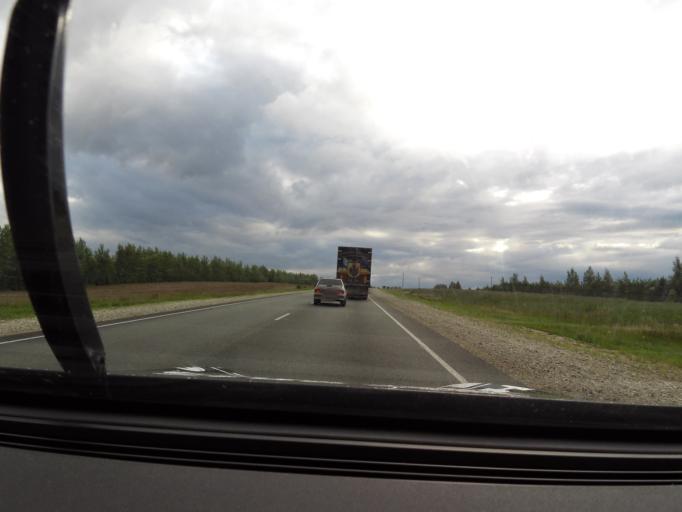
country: RU
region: Tatarstan
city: Nizhniye Vyazovyye
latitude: 55.7234
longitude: 48.4506
